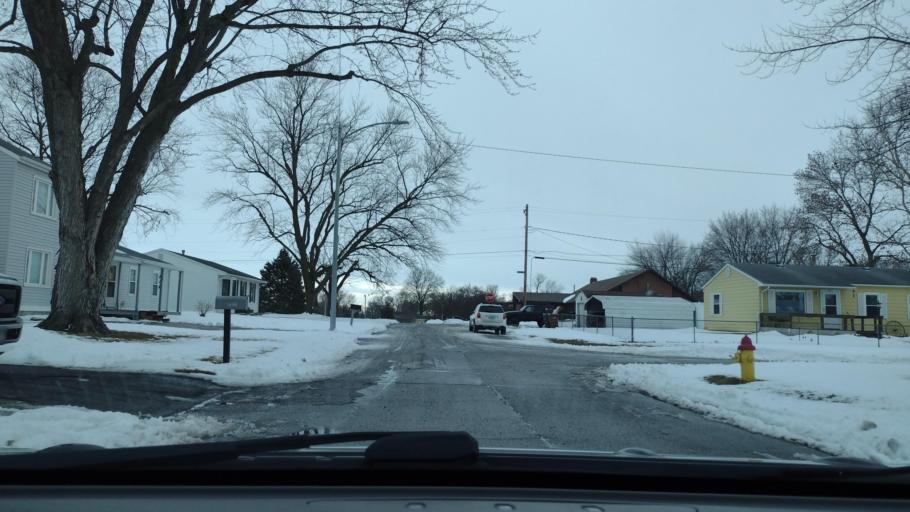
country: US
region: Nebraska
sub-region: Sarpy County
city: La Vista
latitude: 41.1805
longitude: -95.9726
